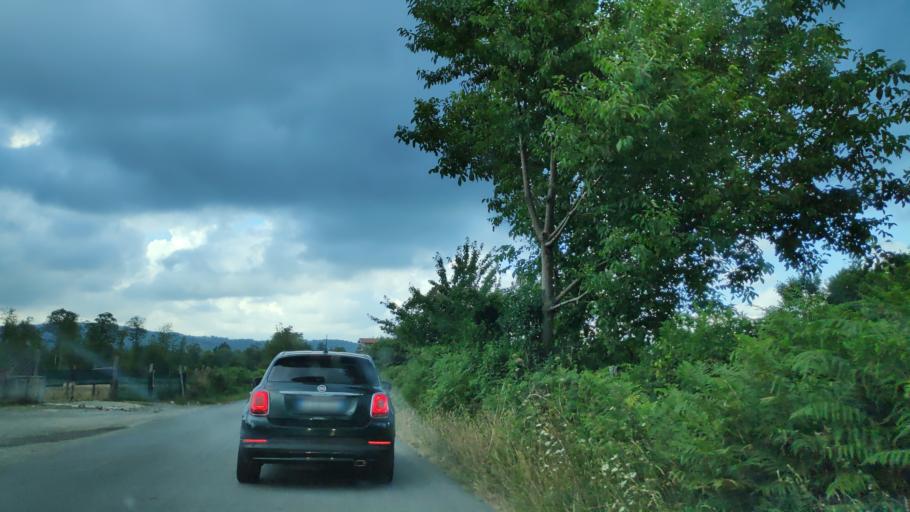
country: IT
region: Calabria
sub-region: Provincia di Vibo-Valentia
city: Serra San Bruno
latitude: 38.5560
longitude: 16.3266
